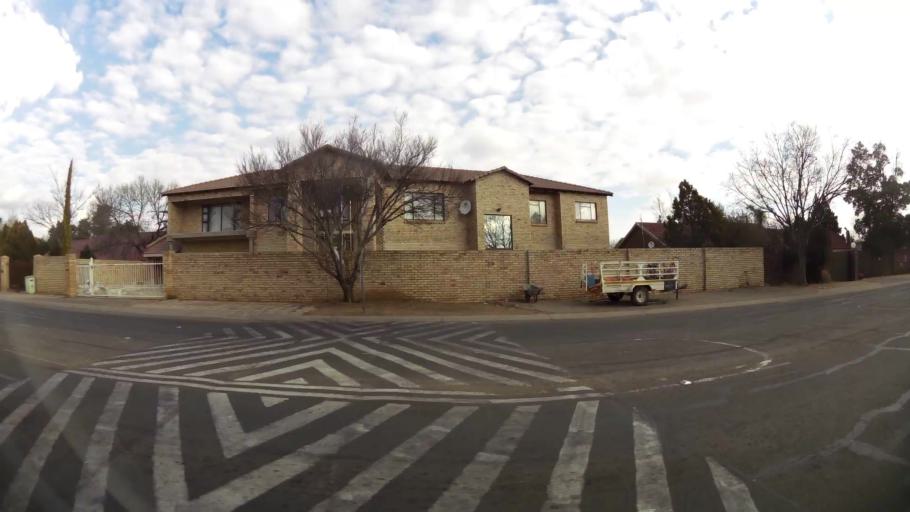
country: ZA
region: Orange Free State
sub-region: Mangaung Metropolitan Municipality
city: Bloemfontein
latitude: -29.0802
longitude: 26.1982
